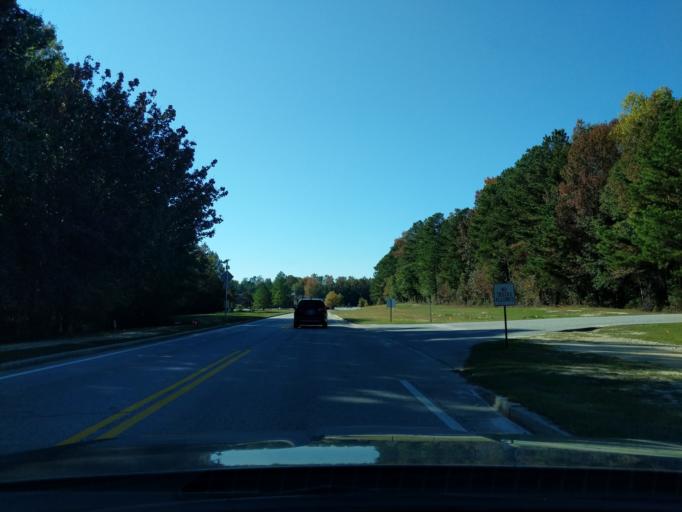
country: US
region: Georgia
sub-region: Columbia County
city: Grovetown
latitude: 33.4665
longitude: -82.1880
